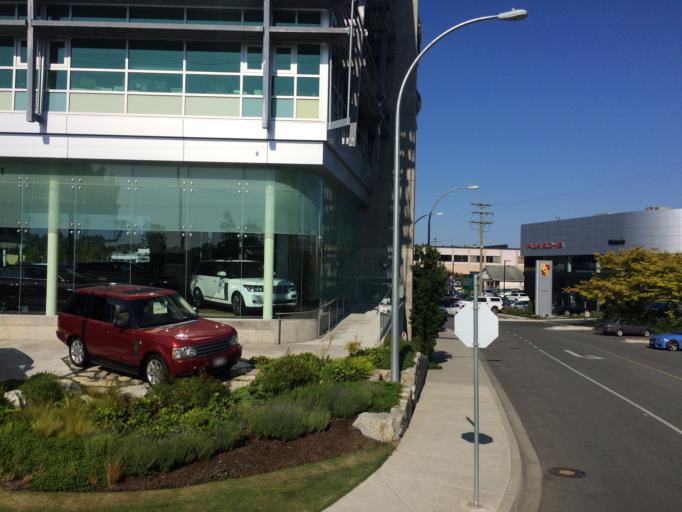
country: CA
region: British Columbia
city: Victoria
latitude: 48.4510
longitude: -123.3743
